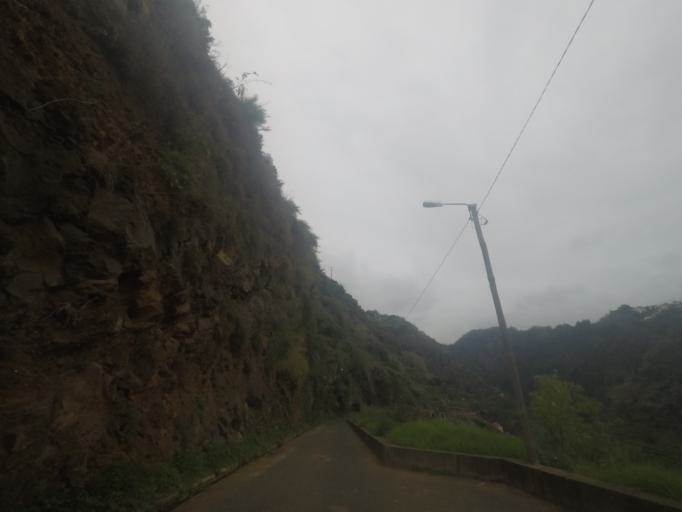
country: PT
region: Madeira
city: Camara de Lobos
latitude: 32.6615
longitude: -16.9621
